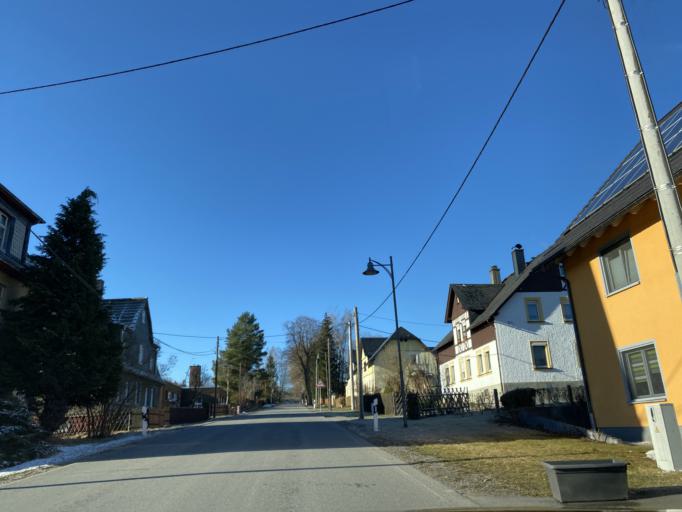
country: DE
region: Saxony
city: Wiesa
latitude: 50.6089
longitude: 13.0068
